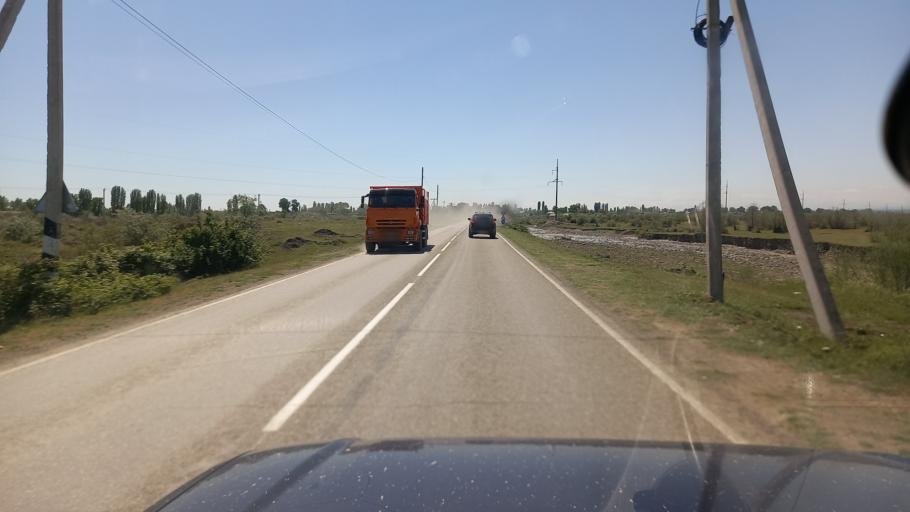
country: RU
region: Dagestan
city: Samur
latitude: 41.7344
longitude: 48.4523
